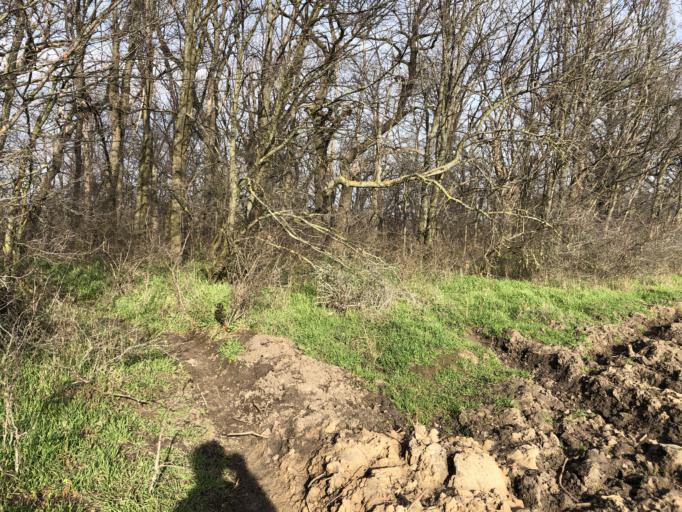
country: DE
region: Saxony-Anhalt
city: Lieskau
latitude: 51.4872
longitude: 11.8579
